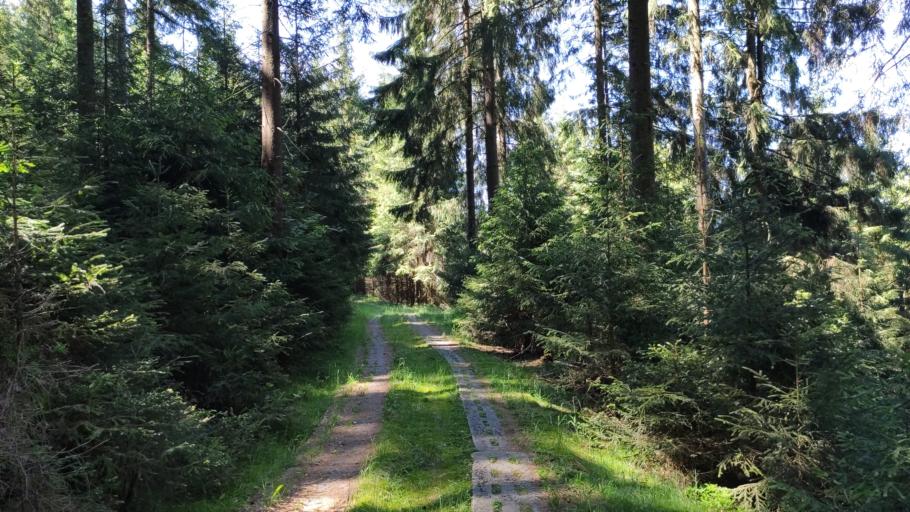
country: DE
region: Bavaria
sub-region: Upper Franconia
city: Tschirn
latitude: 50.4311
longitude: 11.4537
